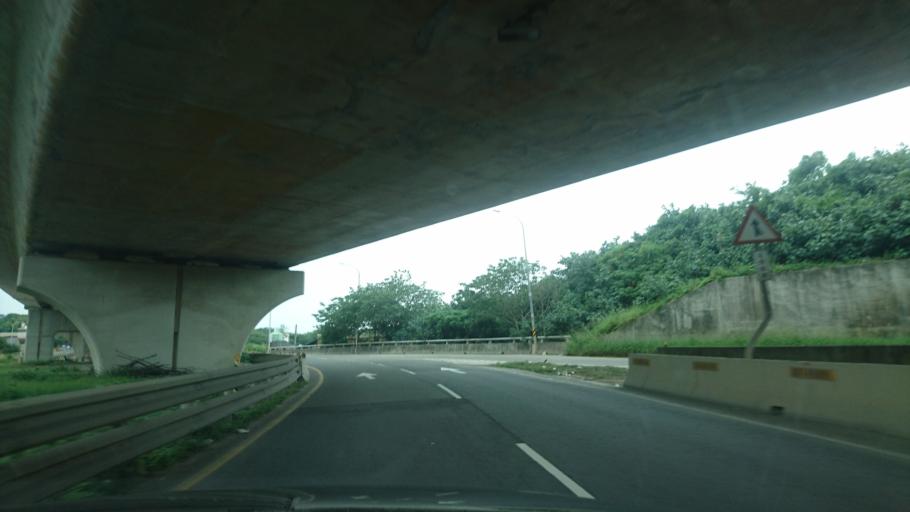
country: TW
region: Taipei
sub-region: Taipei
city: Banqiao
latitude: 25.1387
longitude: 121.3751
